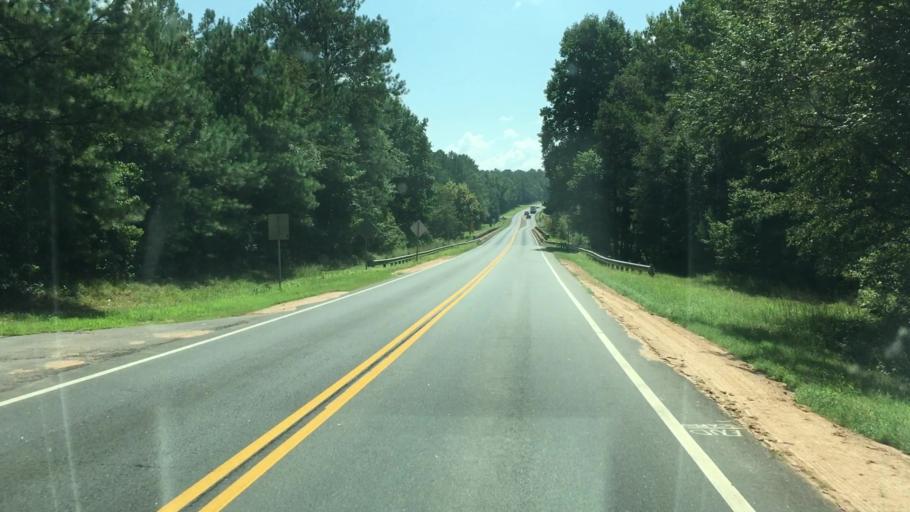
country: US
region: Georgia
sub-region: Morgan County
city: Madison
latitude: 33.7202
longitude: -83.4333
